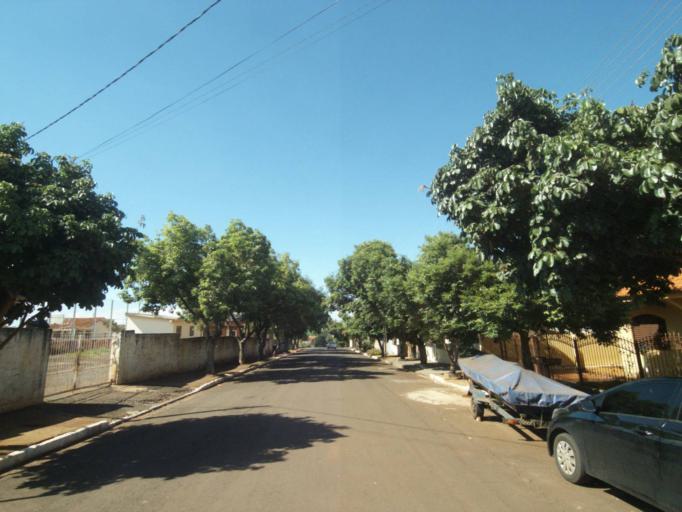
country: BR
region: Parana
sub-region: Sertanopolis
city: Sertanopolis
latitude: -23.0391
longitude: -50.8146
